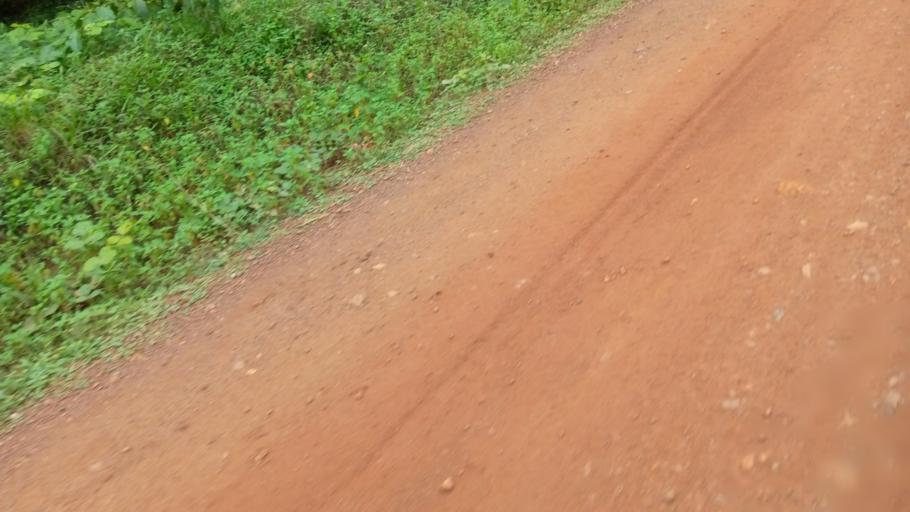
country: SL
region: Southern Province
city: Tongole
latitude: 7.4377
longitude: -11.8454
